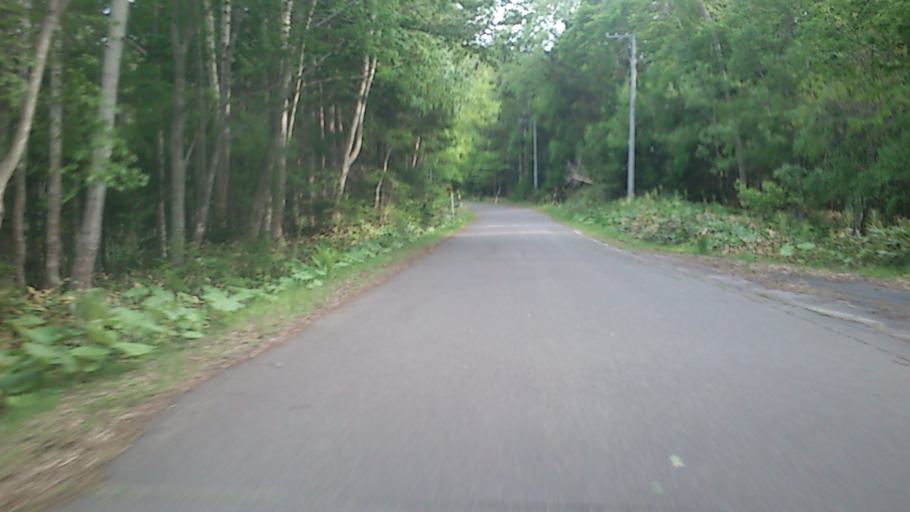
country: JP
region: Hokkaido
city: Bihoro
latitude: 43.4291
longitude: 144.0845
